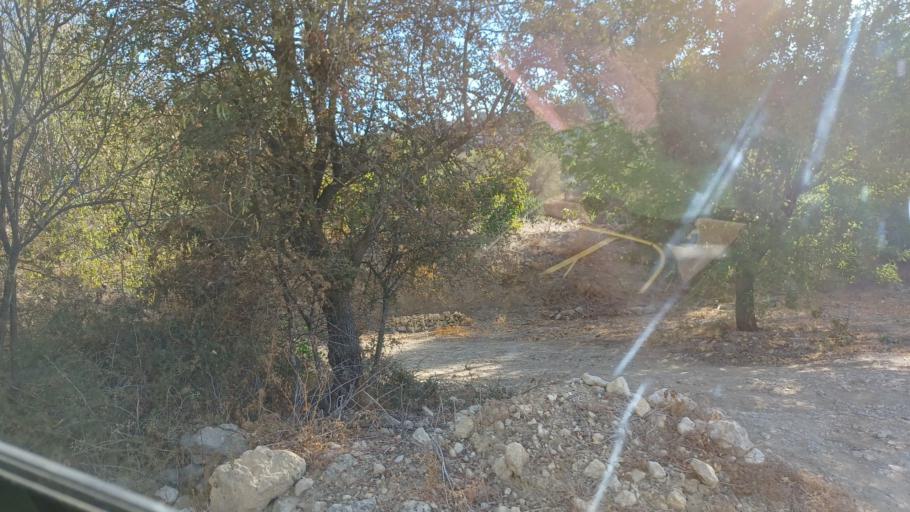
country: CY
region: Pafos
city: Tala
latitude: 34.9255
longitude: 32.4856
